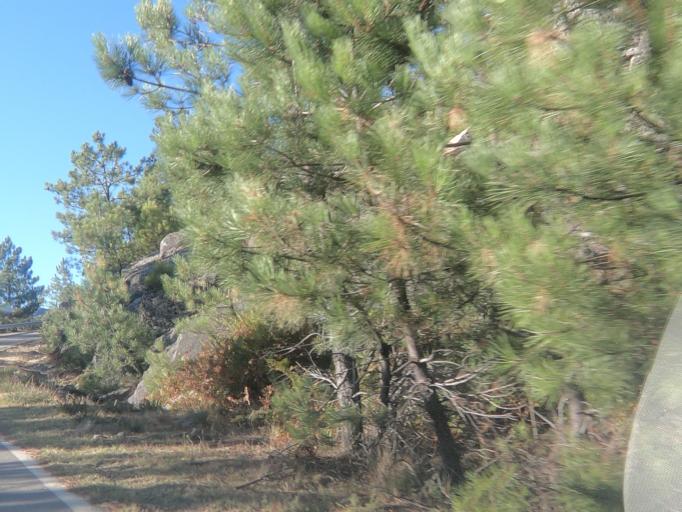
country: PT
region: Vila Real
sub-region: Vila Real
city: Vila Real
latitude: 41.3348
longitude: -7.7891
